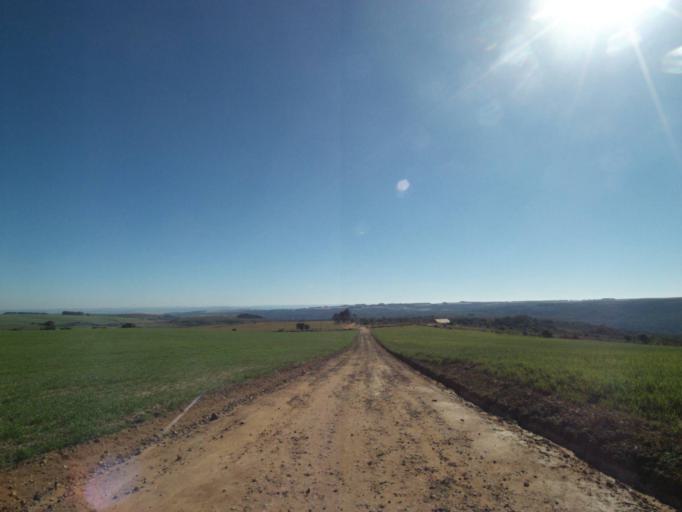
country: BR
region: Parana
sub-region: Tibagi
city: Tibagi
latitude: -24.5727
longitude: -50.2660
